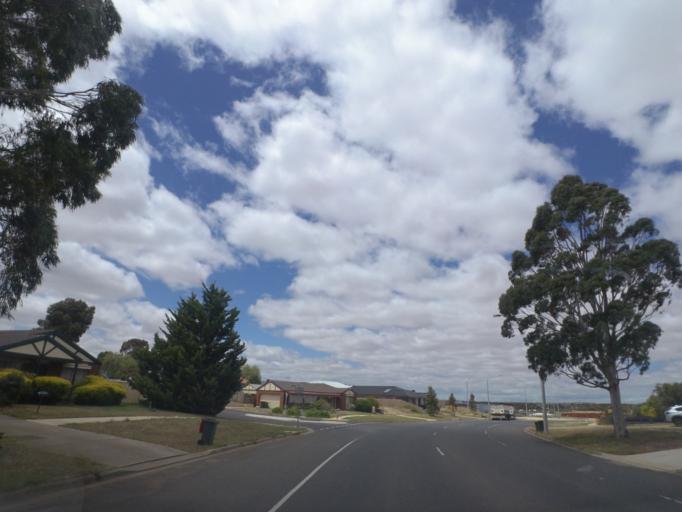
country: AU
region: Victoria
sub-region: Moorabool
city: Bacchus Marsh
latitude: -37.6725
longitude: 144.4235
